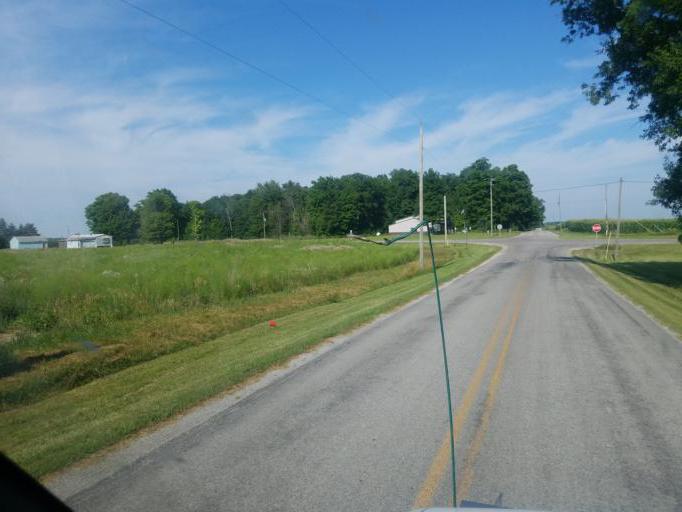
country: US
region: Ohio
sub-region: Logan County
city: Northwood
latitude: 40.5527
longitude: -83.6666
